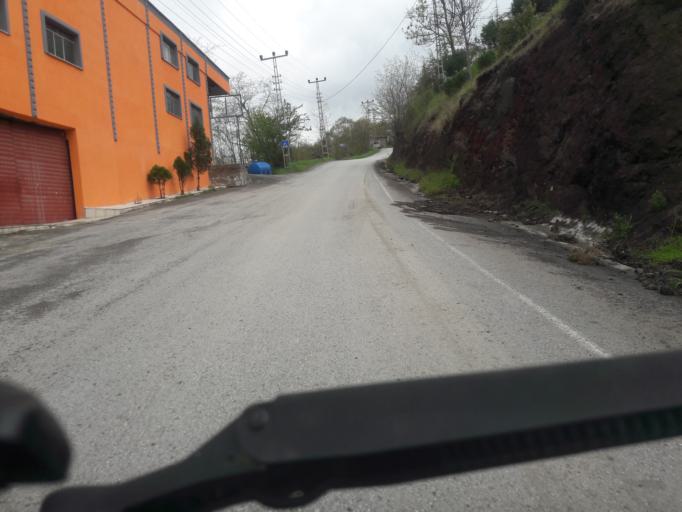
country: TR
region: Trabzon
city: Derecik
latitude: 40.9447
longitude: 39.4970
